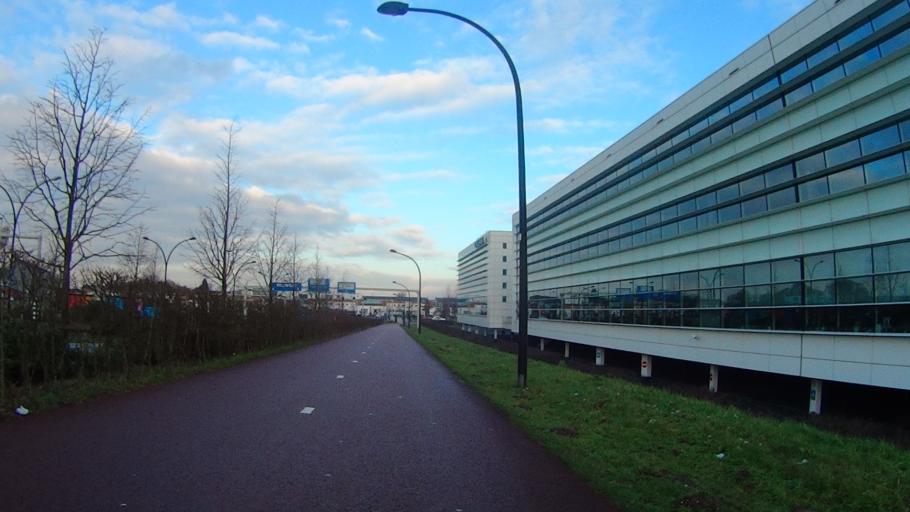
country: NL
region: Utrecht
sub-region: Gemeente Amersfoort
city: Hoogland
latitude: 52.1949
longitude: 5.4061
